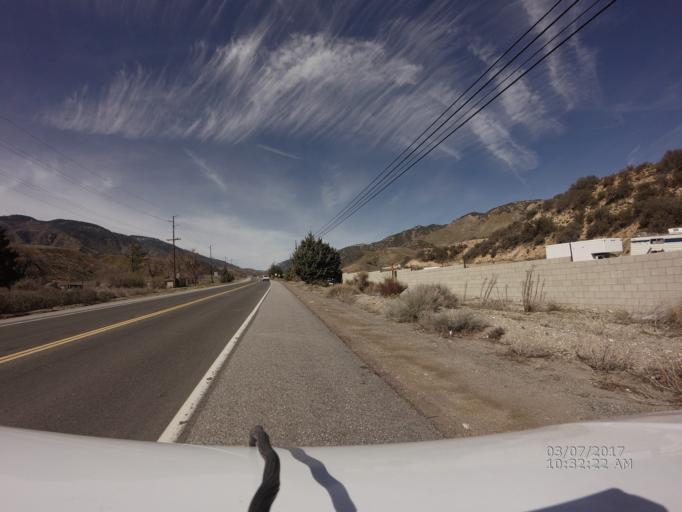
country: US
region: California
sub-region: Kern County
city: Lebec
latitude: 34.8180
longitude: -118.8923
